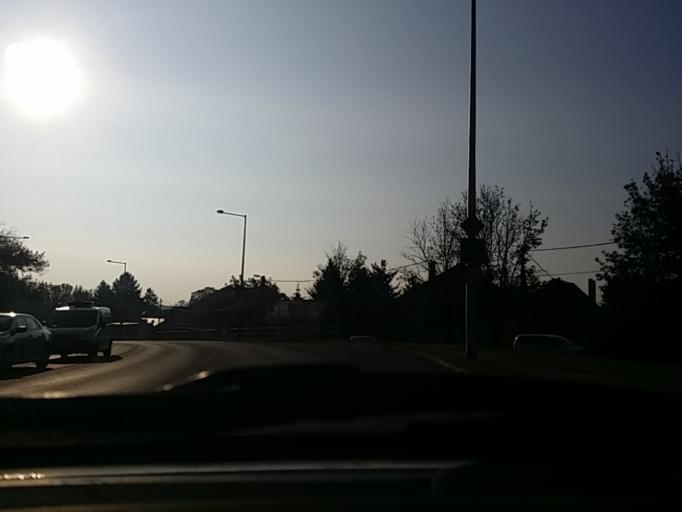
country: HU
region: Pest
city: Szentendre
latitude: 47.6645
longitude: 19.0717
